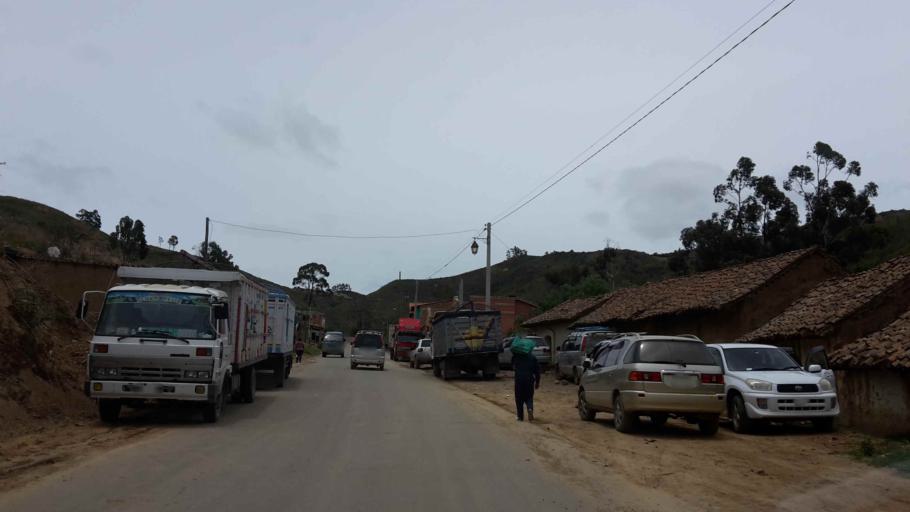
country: BO
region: Cochabamba
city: Totora
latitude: -17.7325
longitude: -65.1900
